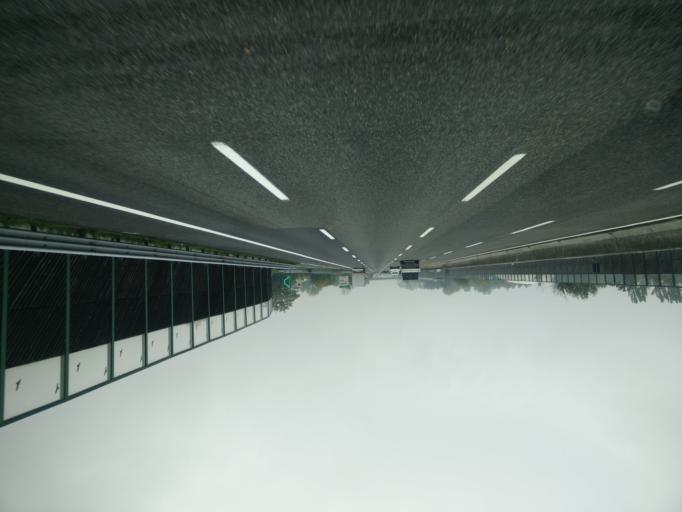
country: IT
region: Emilia-Romagna
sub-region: Provincia di Modena
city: Baggiovara
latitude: 44.6309
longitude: 10.8772
